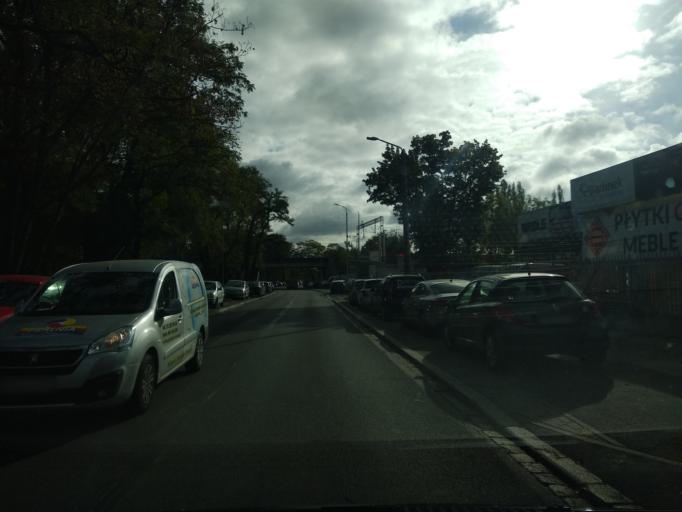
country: PL
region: Lower Silesian Voivodeship
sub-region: Powiat wroclawski
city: Wroclaw
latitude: 51.1127
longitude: 16.9957
